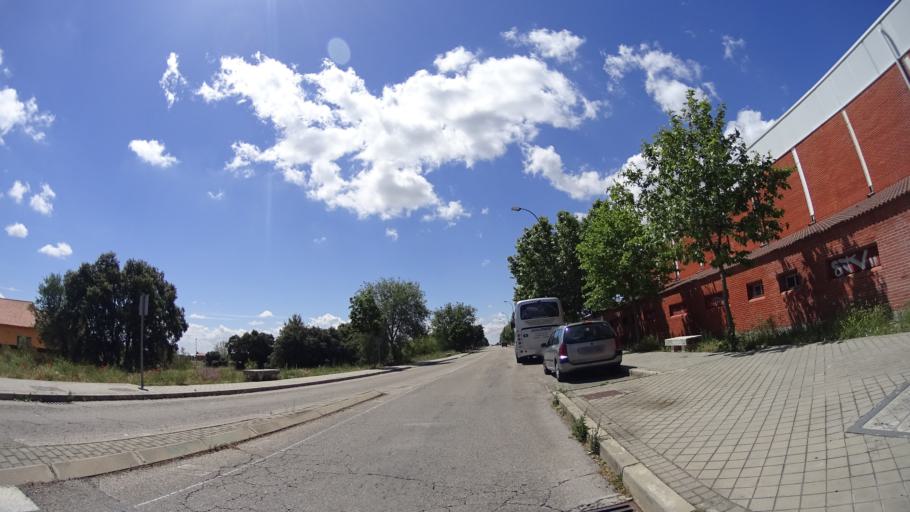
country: ES
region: Madrid
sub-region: Provincia de Madrid
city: Colmenarejo
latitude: 40.5519
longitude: -4.0116
